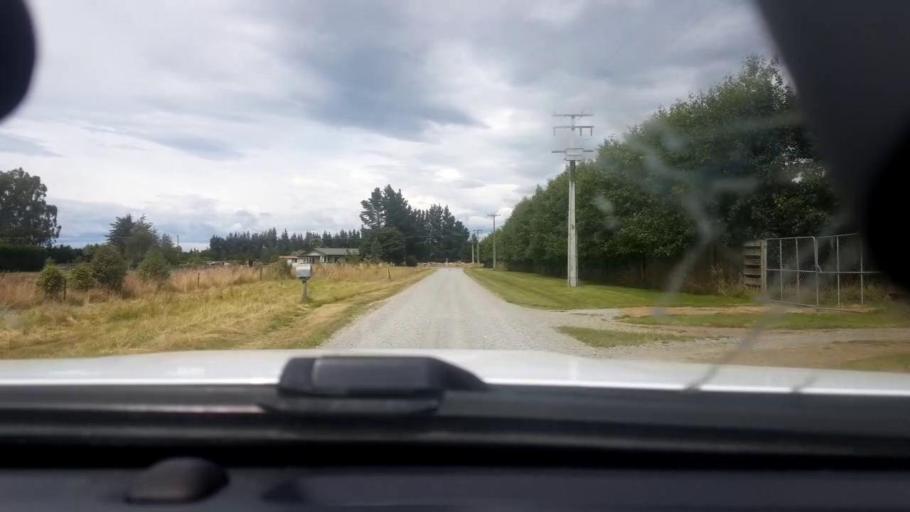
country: NZ
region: Canterbury
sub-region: Timaru District
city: Pleasant Point
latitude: -44.1431
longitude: 171.2890
